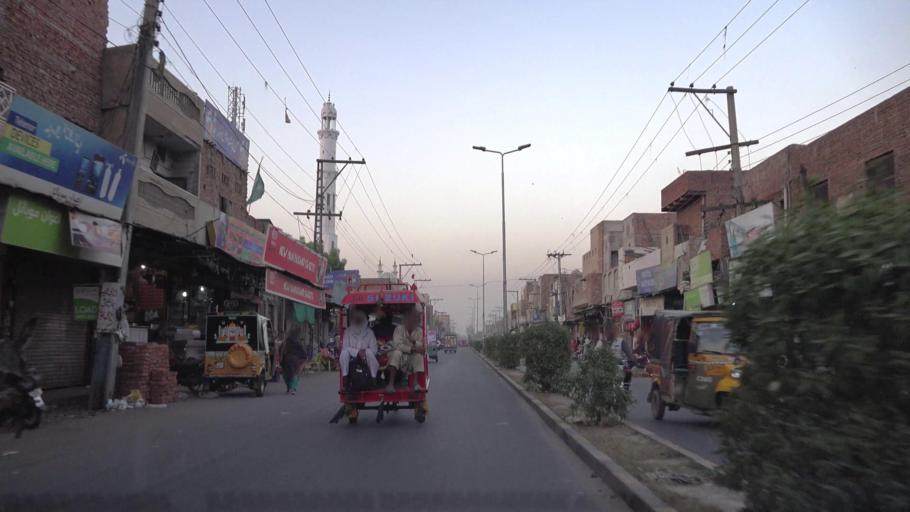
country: PK
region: Punjab
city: Faisalabad
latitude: 31.4440
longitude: 73.0955
